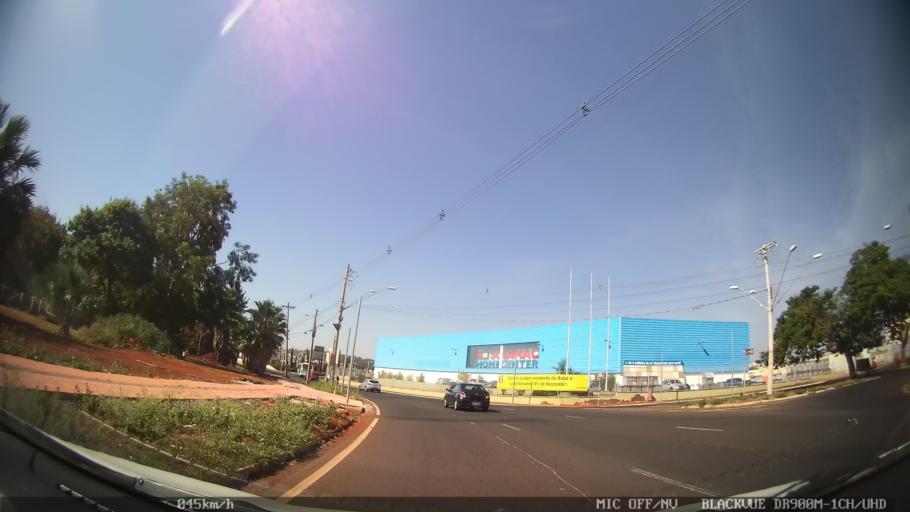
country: BR
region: Sao Paulo
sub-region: Ribeirao Preto
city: Ribeirao Preto
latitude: -21.1671
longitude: -47.8153
